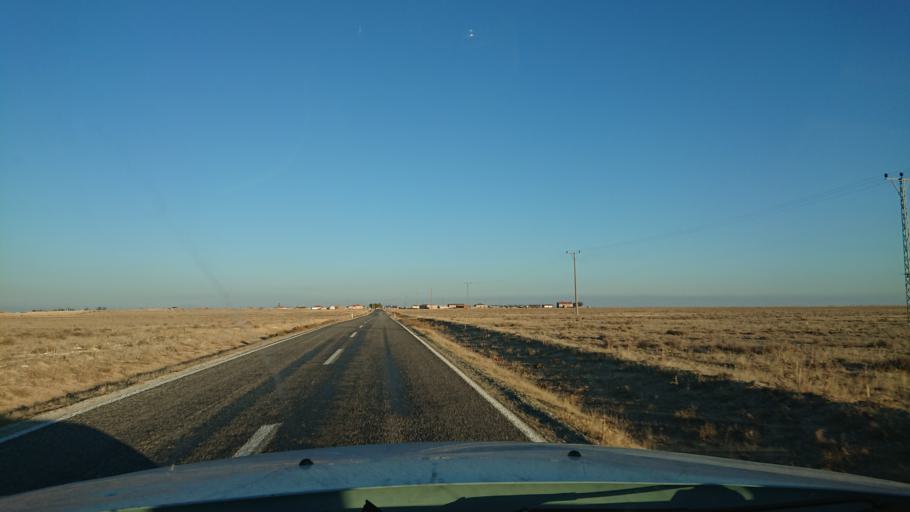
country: TR
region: Aksaray
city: Eskil
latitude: 38.4641
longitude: 33.2395
